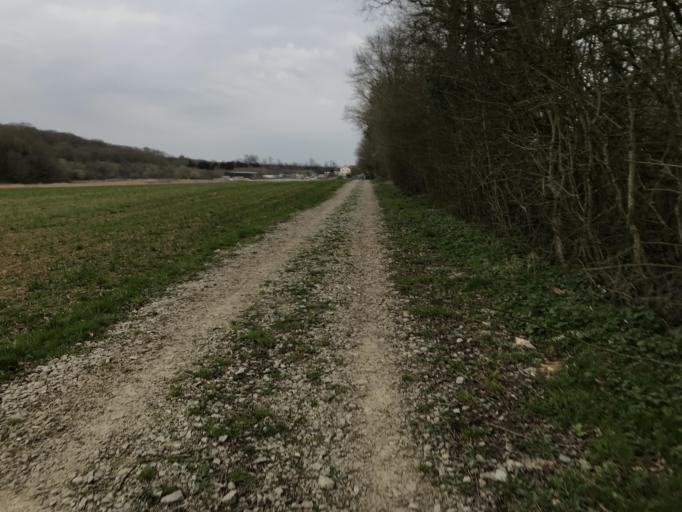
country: FR
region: Ile-de-France
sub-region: Departement de l'Essonne
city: Limours
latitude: 48.6480
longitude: 2.0536
